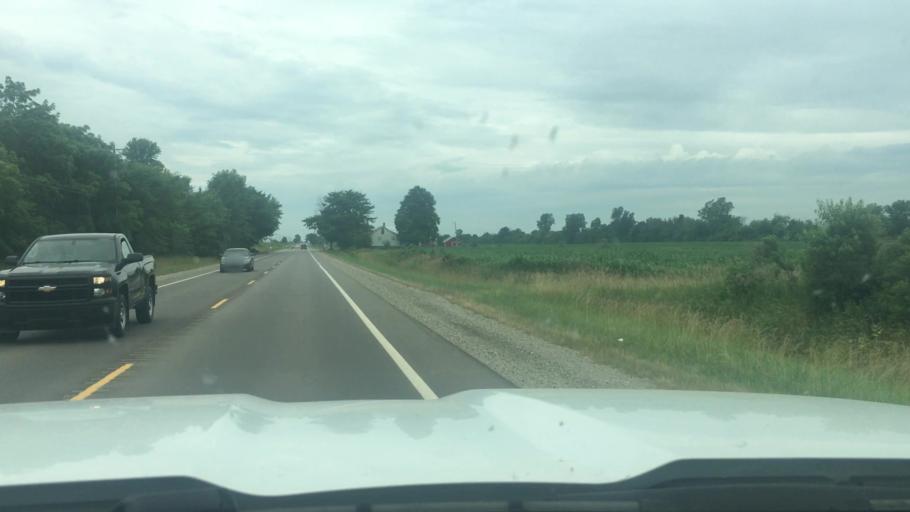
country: US
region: Michigan
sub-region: Clinton County
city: Fowler
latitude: 43.0018
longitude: -84.6848
